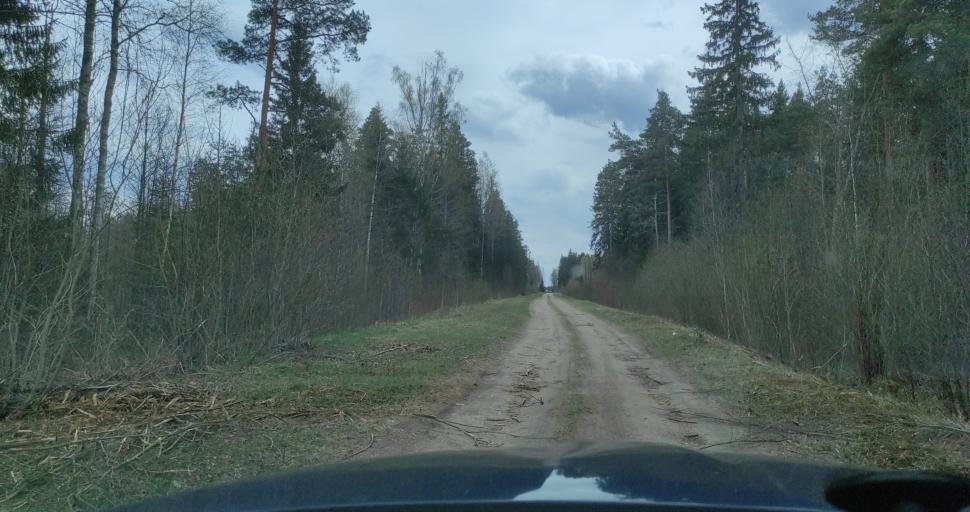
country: LV
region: Dundaga
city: Dundaga
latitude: 57.3615
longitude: 22.1508
